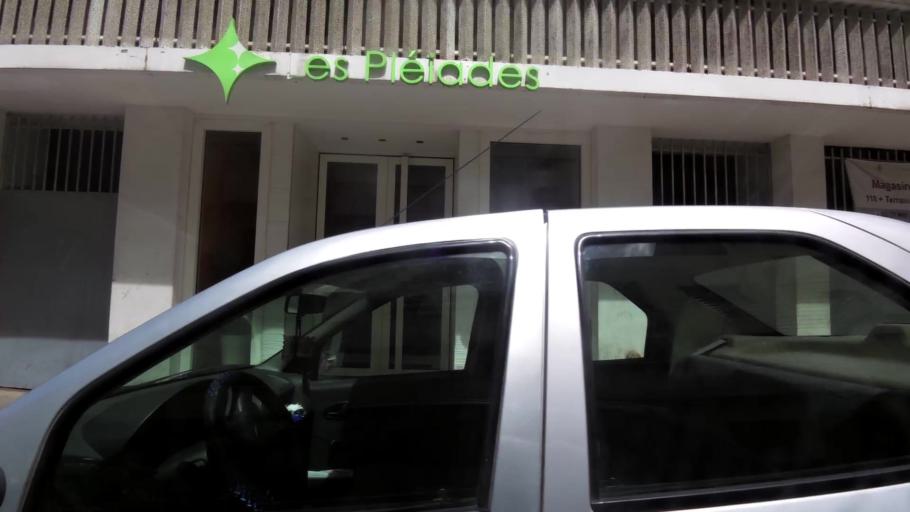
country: MA
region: Grand Casablanca
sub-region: Casablanca
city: Casablanca
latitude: 33.5971
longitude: -7.6361
